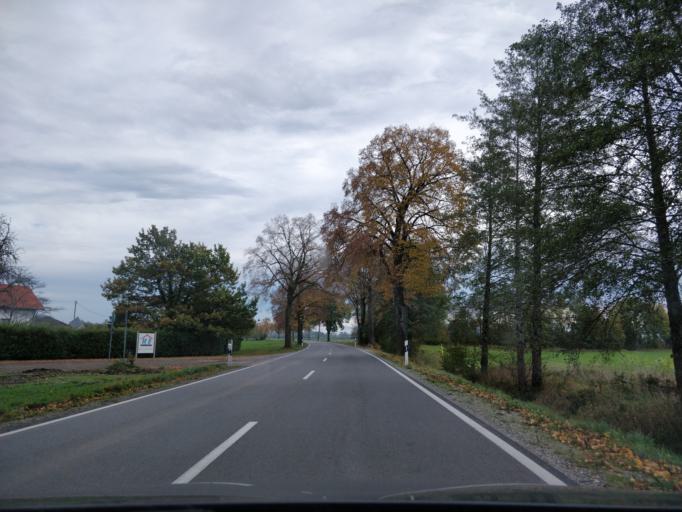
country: DE
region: Bavaria
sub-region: Swabia
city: Wiedergeltingen
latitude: 48.0345
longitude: 10.6850
